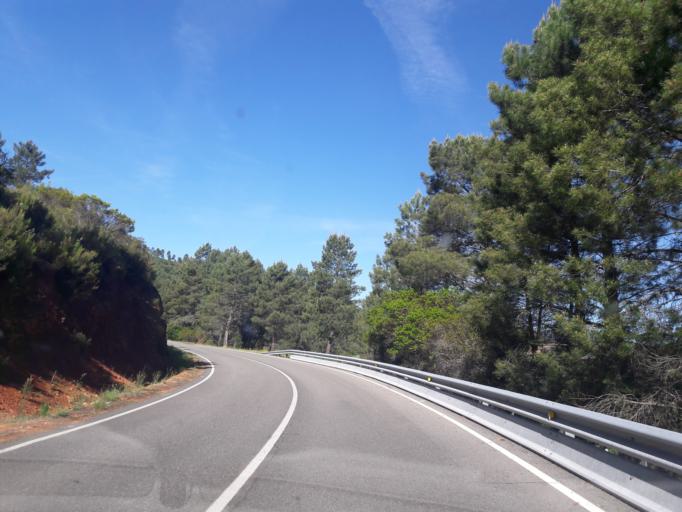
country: ES
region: Castille and Leon
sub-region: Provincia de Salamanca
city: Herguijuela de la Sierra
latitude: 40.4135
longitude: -6.1057
